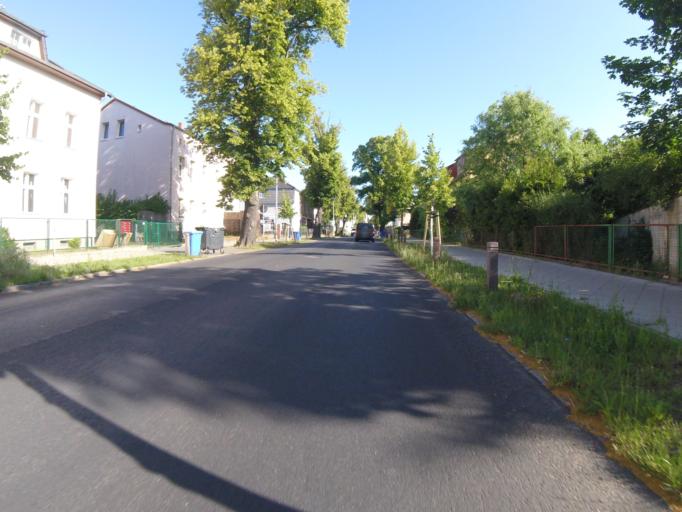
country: DE
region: Brandenburg
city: Konigs Wusterhausen
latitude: 52.2933
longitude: 13.6263
